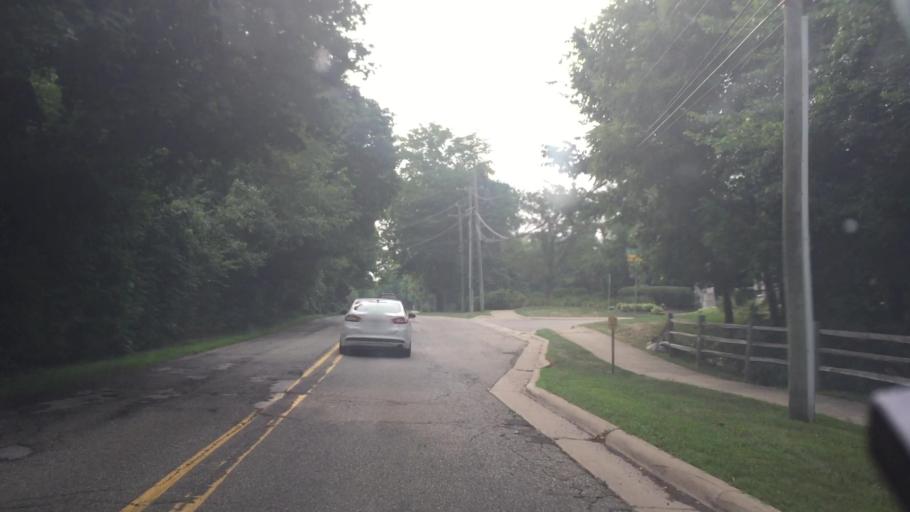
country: US
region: Michigan
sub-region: Oakland County
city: Bloomfield Hills
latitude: 42.5964
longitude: -83.2524
